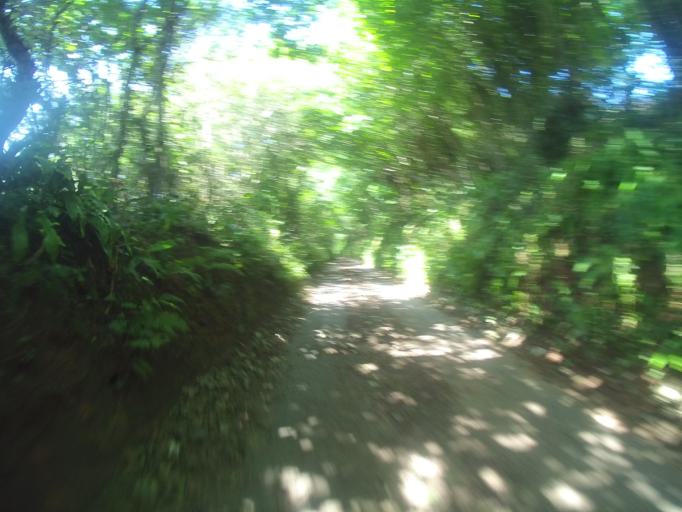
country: GB
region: England
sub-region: Devon
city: Dartmouth
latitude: 50.3619
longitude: -3.6194
